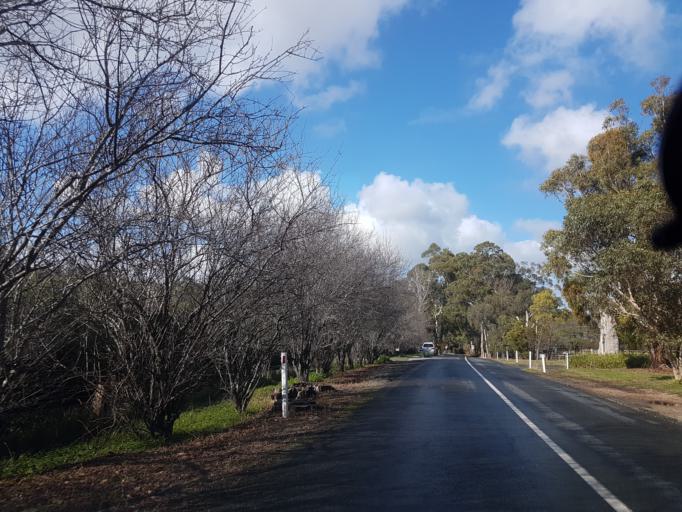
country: AU
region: South Australia
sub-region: Adelaide Hills
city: Heathfield
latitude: -35.0411
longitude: 138.7083
